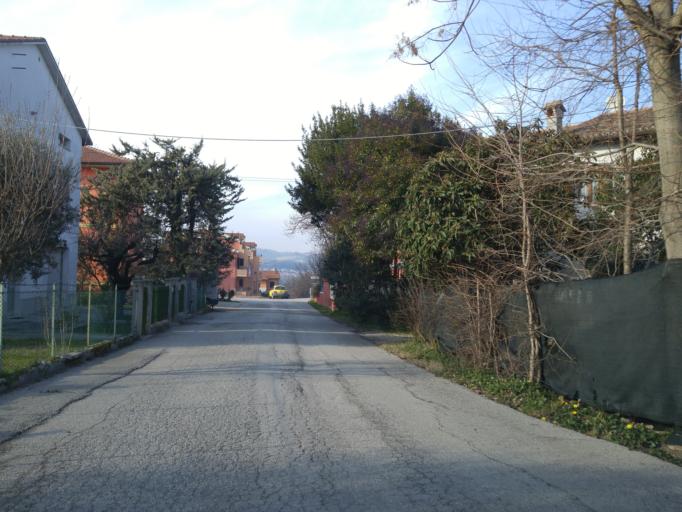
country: IT
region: The Marches
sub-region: Provincia di Pesaro e Urbino
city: Villanova
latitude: 43.7429
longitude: 12.9364
